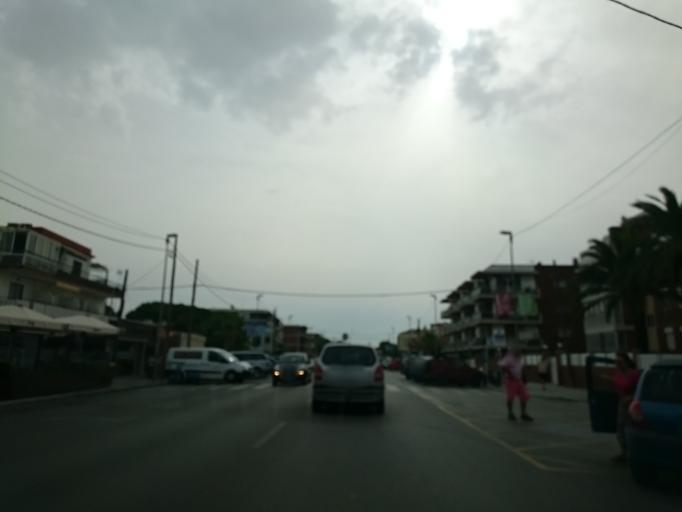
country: ES
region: Catalonia
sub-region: Provincia de Barcelona
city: Castelldefels
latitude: 41.2658
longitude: 1.9643
